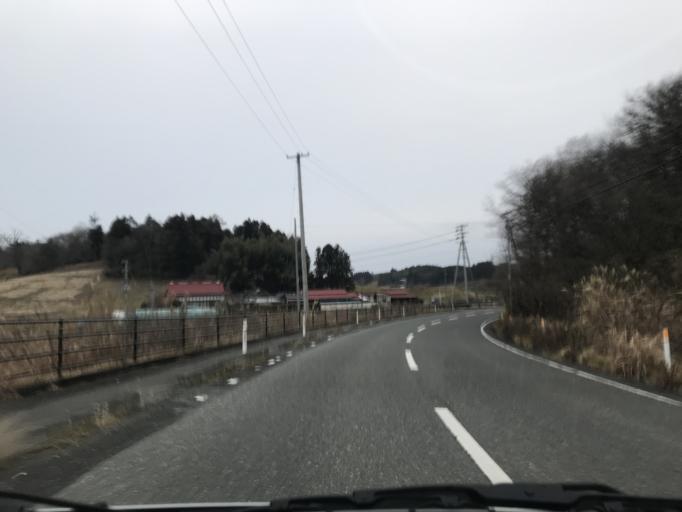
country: JP
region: Miyagi
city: Kogota
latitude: 38.6773
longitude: 141.0997
